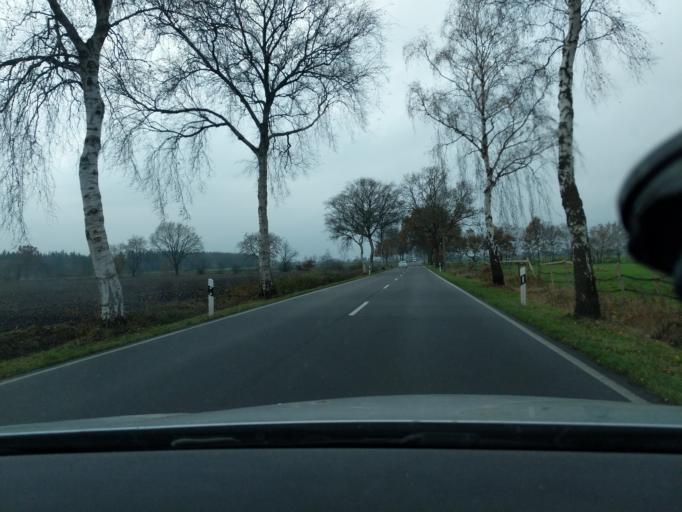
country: DE
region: Lower Saxony
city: Ahlerstedt
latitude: 53.3740
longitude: 9.4504
